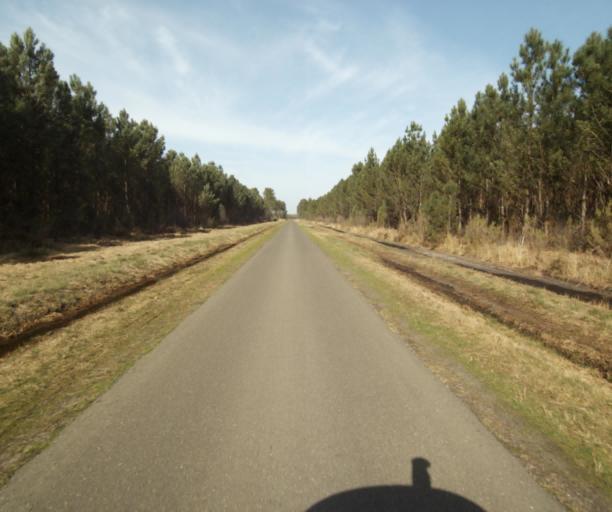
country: FR
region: Aquitaine
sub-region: Departement des Landes
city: Roquefort
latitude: 44.2066
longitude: -0.2005
